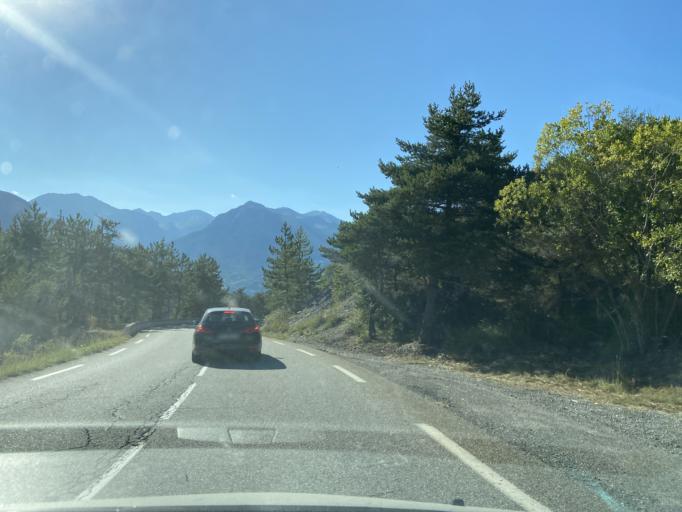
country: FR
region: Provence-Alpes-Cote d'Azur
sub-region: Departement des Hautes-Alpes
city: Guillestre
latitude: 44.6415
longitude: 6.6644
